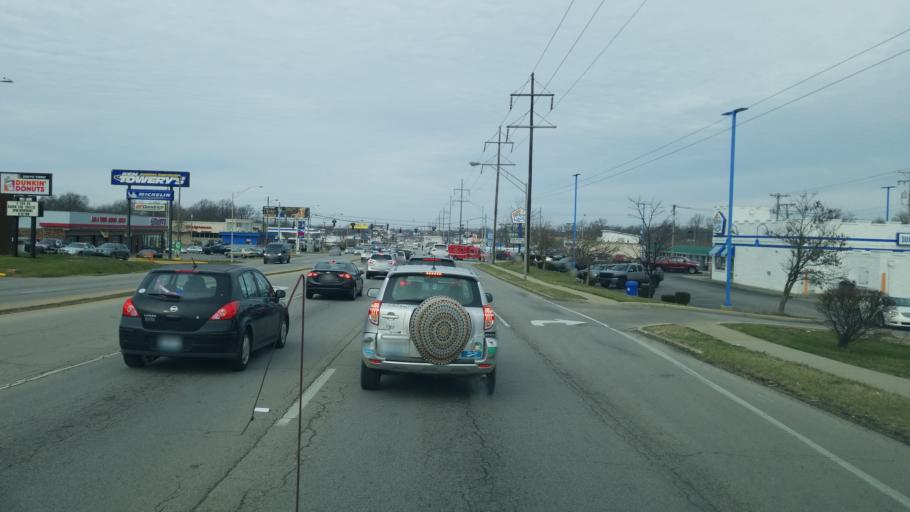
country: US
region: Kentucky
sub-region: Fayette County
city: Lexington-Fayette
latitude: 38.0592
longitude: -84.4639
